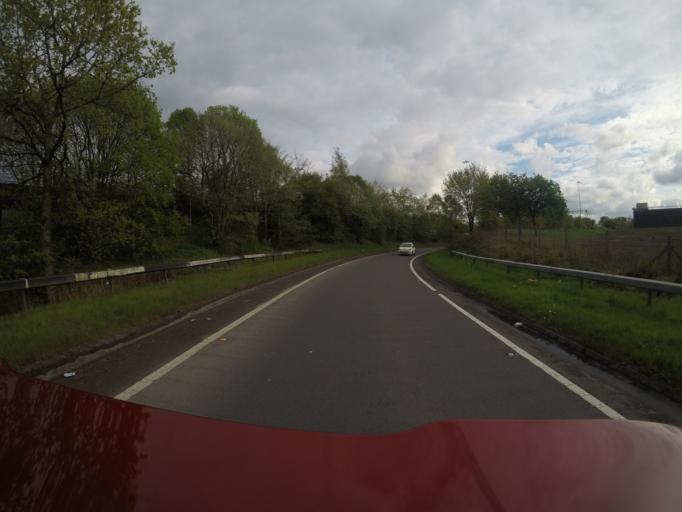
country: GB
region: Scotland
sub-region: West Dunbartonshire
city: Old Kilpatrick
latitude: 55.9248
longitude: -4.4493
